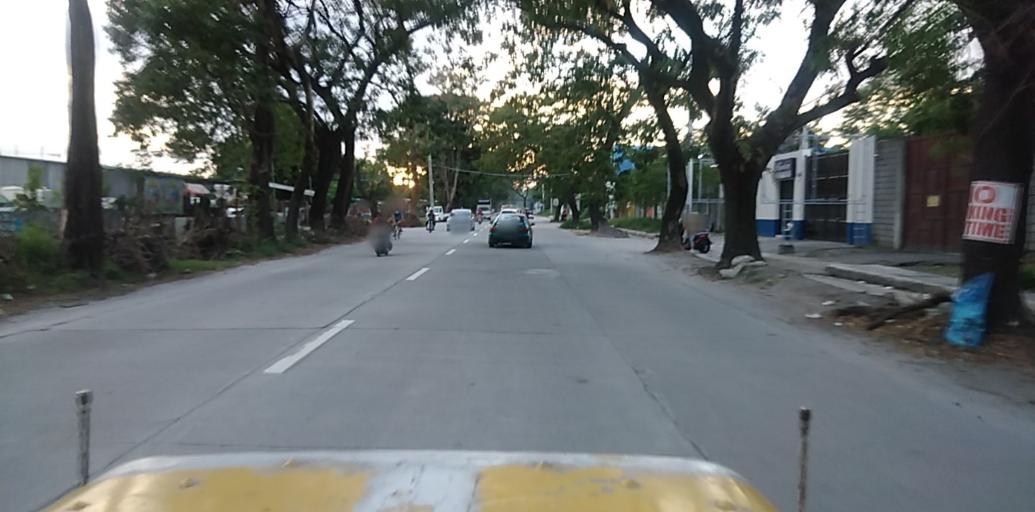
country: PH
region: Central Luzon
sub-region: Province of Pampanga
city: Calibutbut
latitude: 15.1170
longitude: 120.6019
